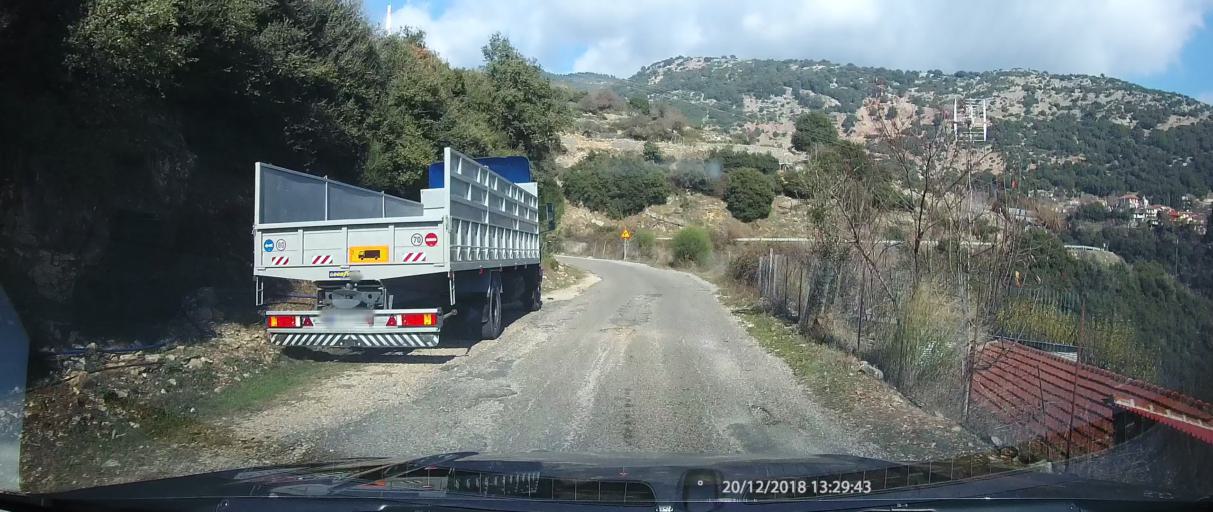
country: GR
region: West Greece
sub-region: Nomos Aitolias kai Akarnanias
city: Paravola
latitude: 38.6310
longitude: 21.5805
